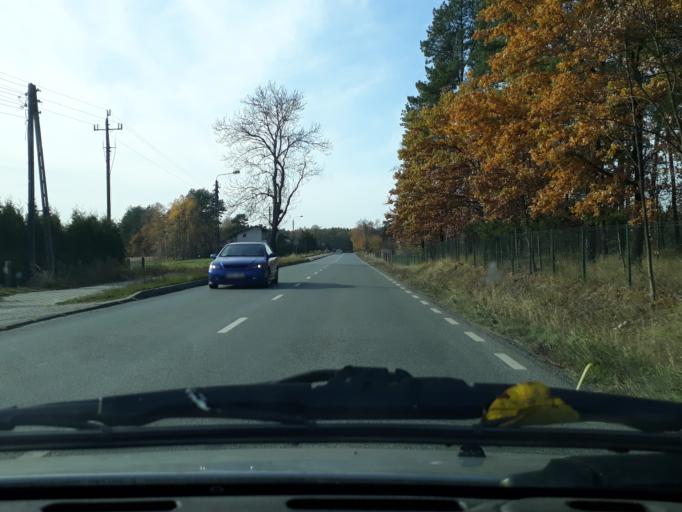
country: PL
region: Silesian Voivodeship
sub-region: Powiat lubliniecki
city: Psary
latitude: 50.5765
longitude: 18.9767
